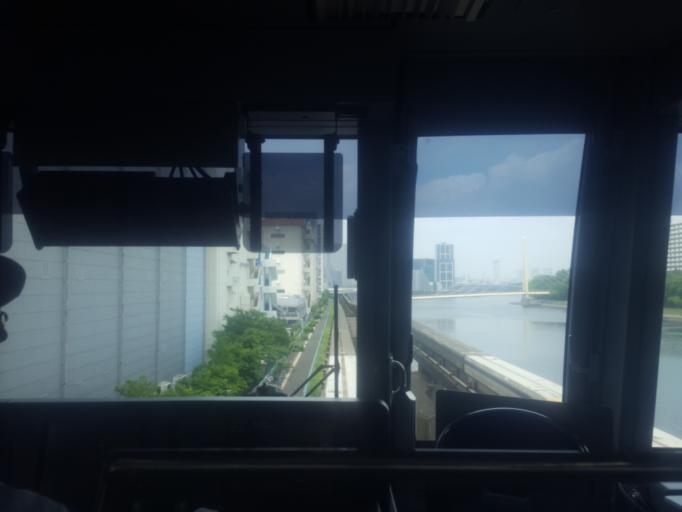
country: JP
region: Kanagawa
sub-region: Kawasaki-shi
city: Kawasaki
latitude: 35.5959
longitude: 139.7471
